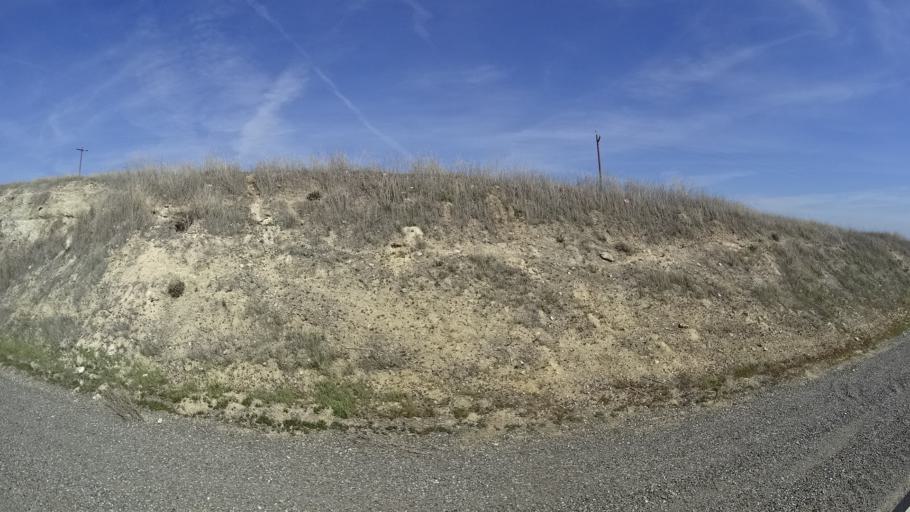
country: US
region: California
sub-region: Glenn County
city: Willows
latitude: 39.5311
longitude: -122.3253
